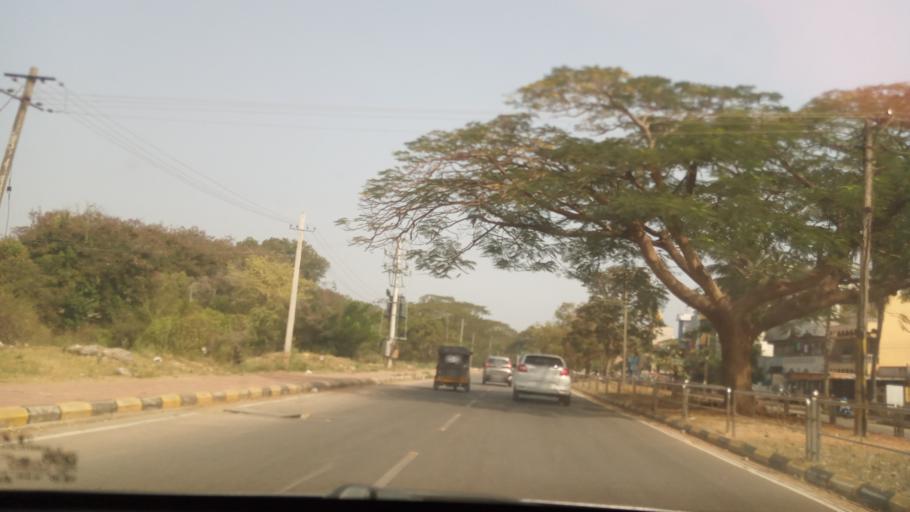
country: IN
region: Karnataka
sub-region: Mysore
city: Mysore
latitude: 12.3037
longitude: 76.6266
